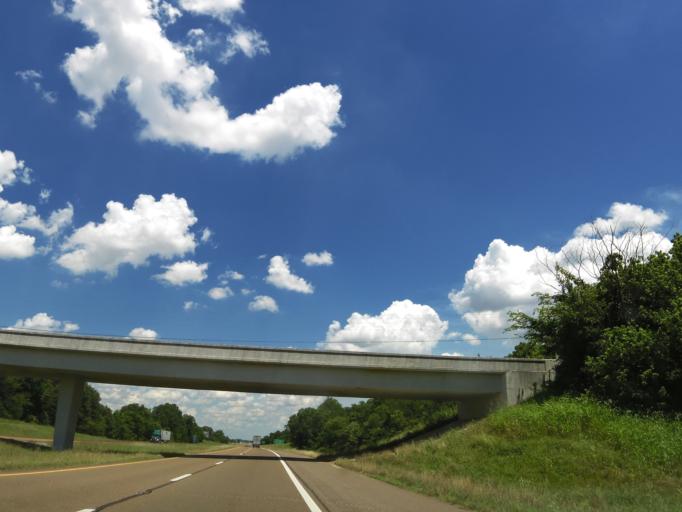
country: US
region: Tennessee
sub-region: Dyer County
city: Dyersburg
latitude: 36.0690
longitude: -89.4186
